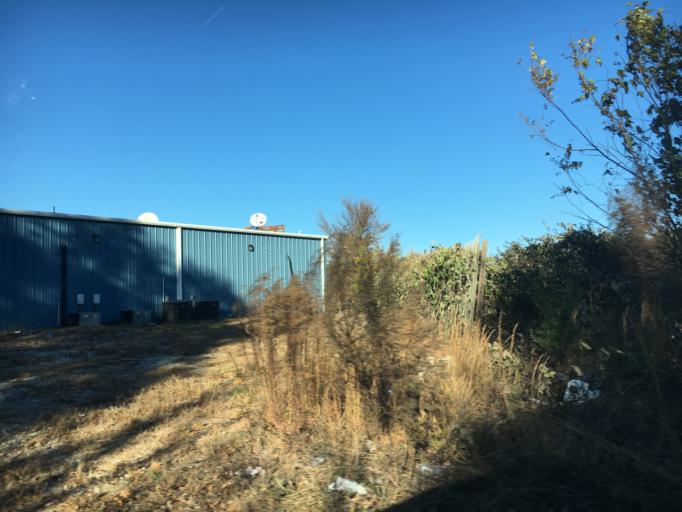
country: US
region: South Carolina
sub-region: Spartanburg County
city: Duncan
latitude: 34.9540
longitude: -82.1683
